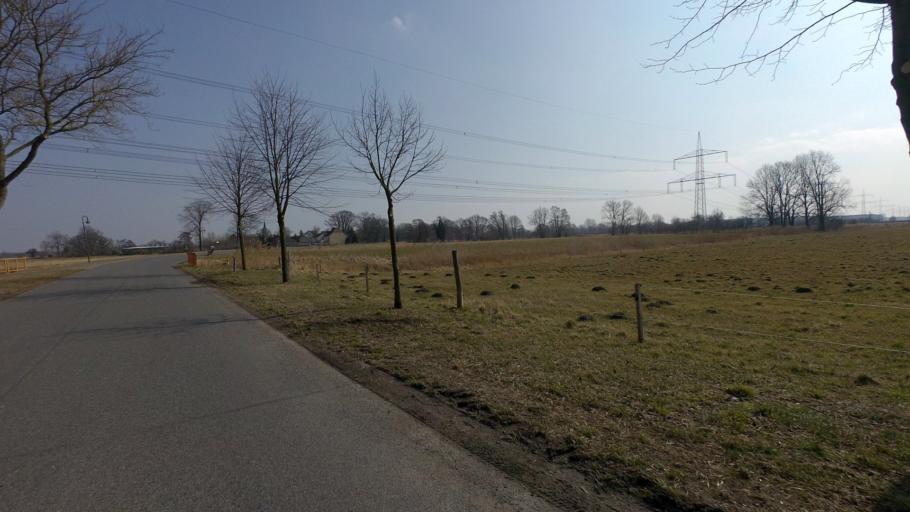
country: DE
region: Brandenburg
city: Gross Kreutz
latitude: 52.4171
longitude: 12.7954
